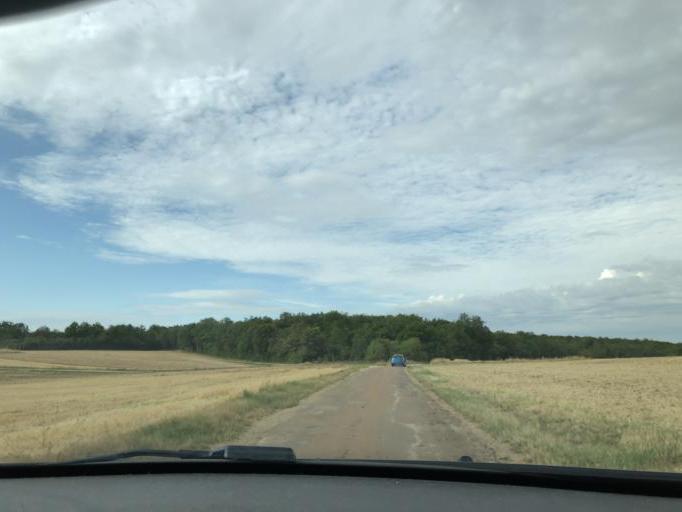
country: FR
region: Bourgogne
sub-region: Departement de l'Yonne
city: Chablis
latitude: 47.7798
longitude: 3.8295
